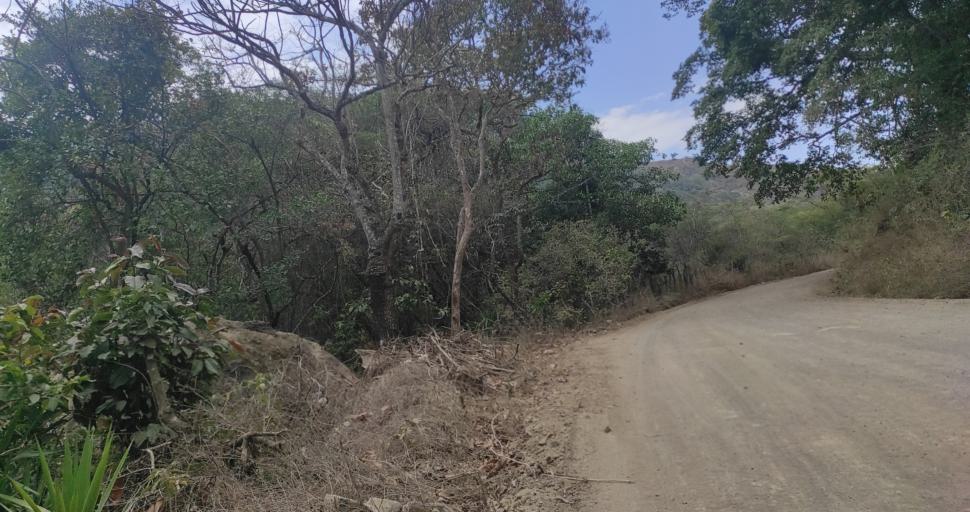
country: EC
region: Loja
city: Catacocha
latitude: -4.0293
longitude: -79.6424
